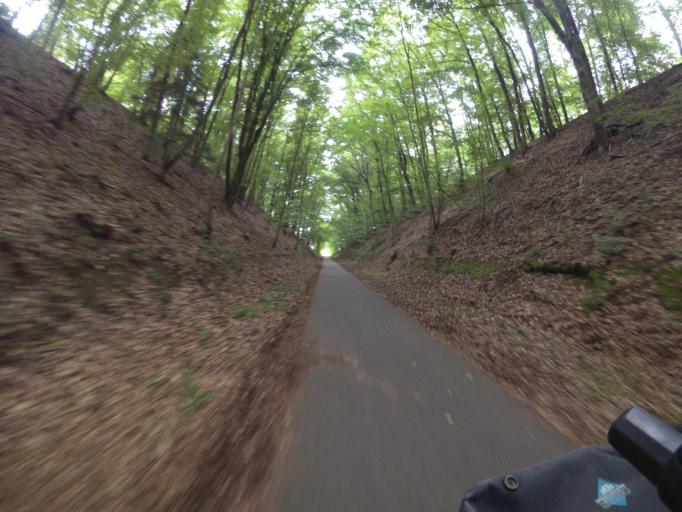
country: DE
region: Rheinland-Pfalz
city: Reichenbach-Steegen
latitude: 49.4891
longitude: 7.5630
